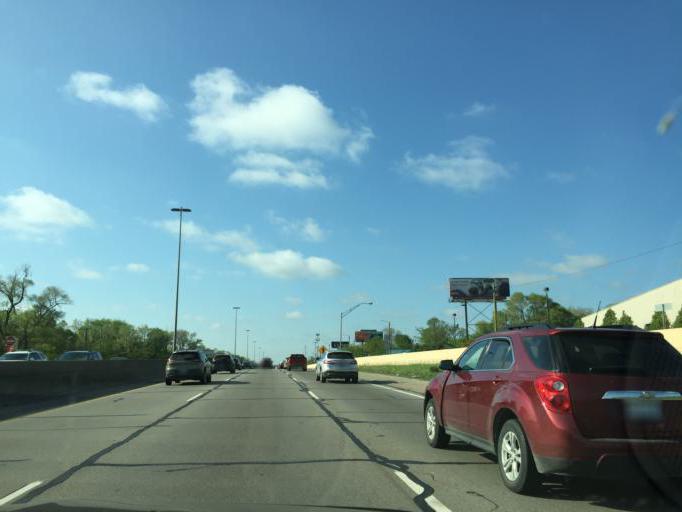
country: US
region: Michigan
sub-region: Wayne County
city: Dearborn
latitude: 42.3711
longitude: -83.2168
